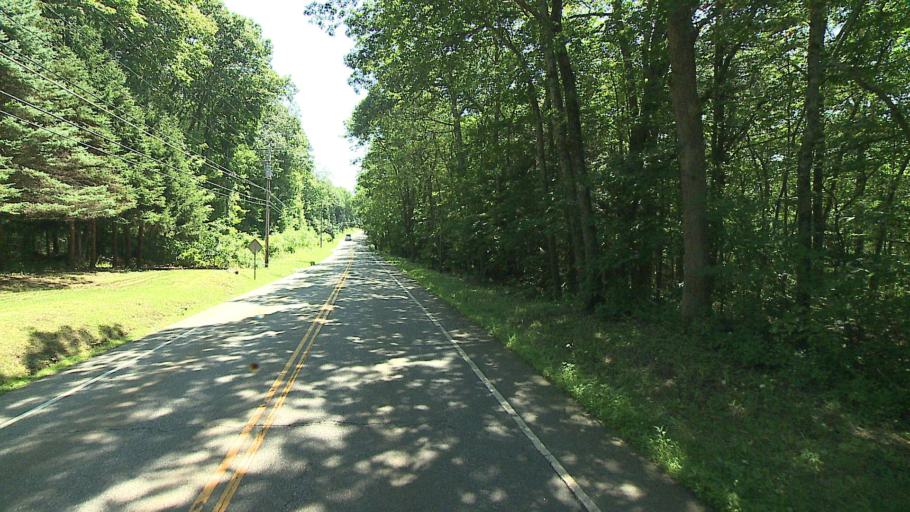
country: US
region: Connecticut
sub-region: Litchfield County
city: Litchfield
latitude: 41.8455
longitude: -73.2855
